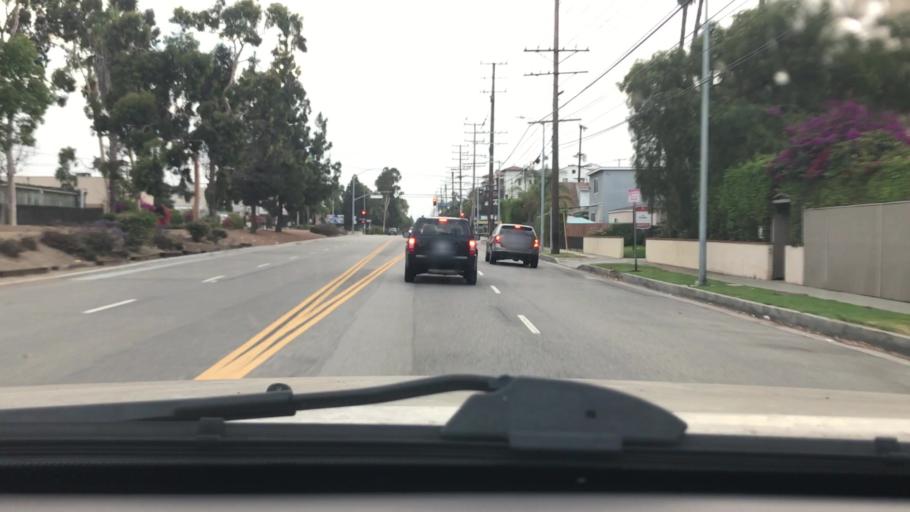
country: US
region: California
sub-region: Los Angeles County
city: Culver City
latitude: 33.9938
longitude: -118.4187
